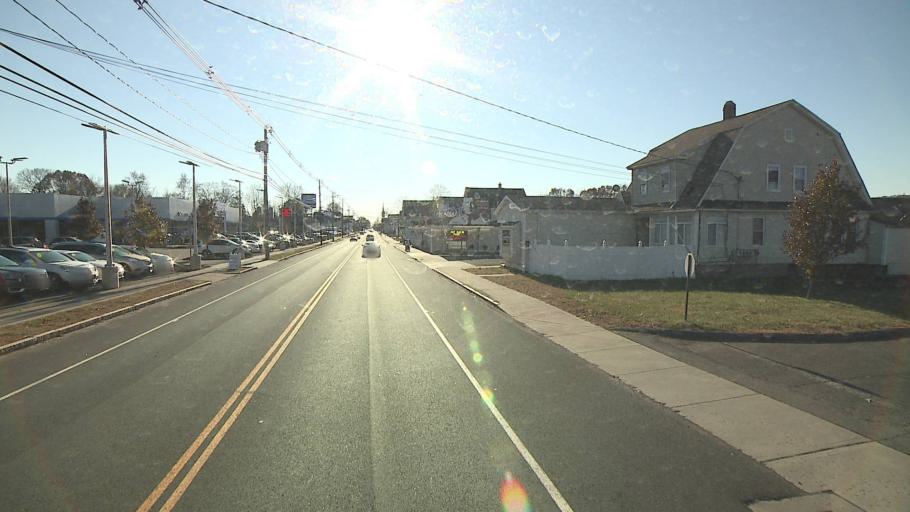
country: US
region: Connecticut
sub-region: New Haven County
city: Wallingford
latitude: 41.4655
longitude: -72.8191
